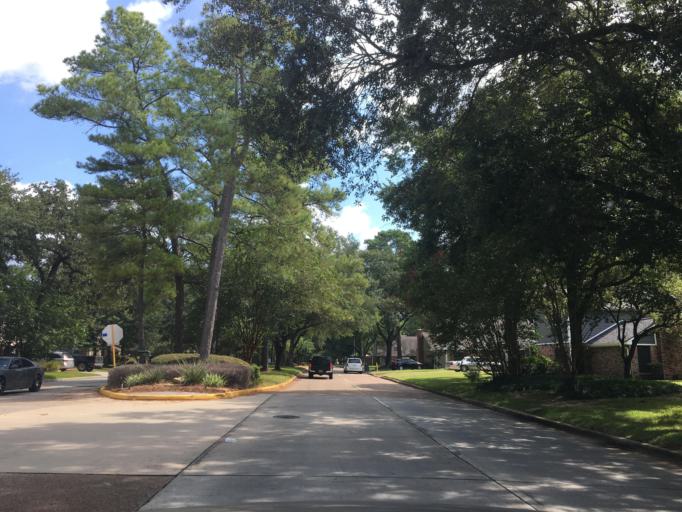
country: US
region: Texas
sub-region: Harris County
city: Spring
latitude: 30.0468
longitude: -95.4425
